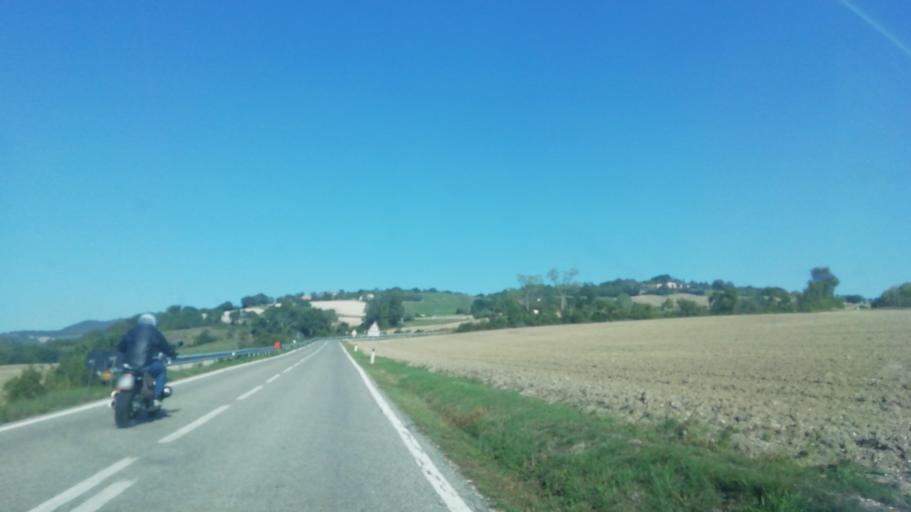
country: IT
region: The Marches
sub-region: Provincia di Pesaro e Urbino
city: Frontone
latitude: 43.5440
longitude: 12.7170
